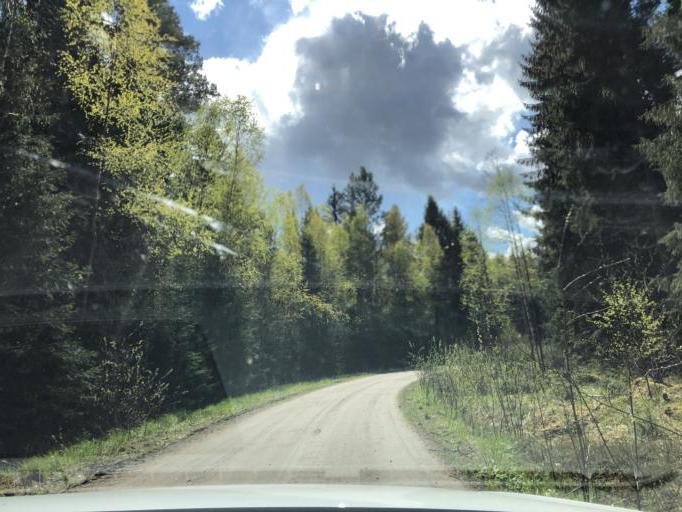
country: SE
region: Uppsala
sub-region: Heby Kommun
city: Tarnsjo
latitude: 60.2610
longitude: 16.9164
